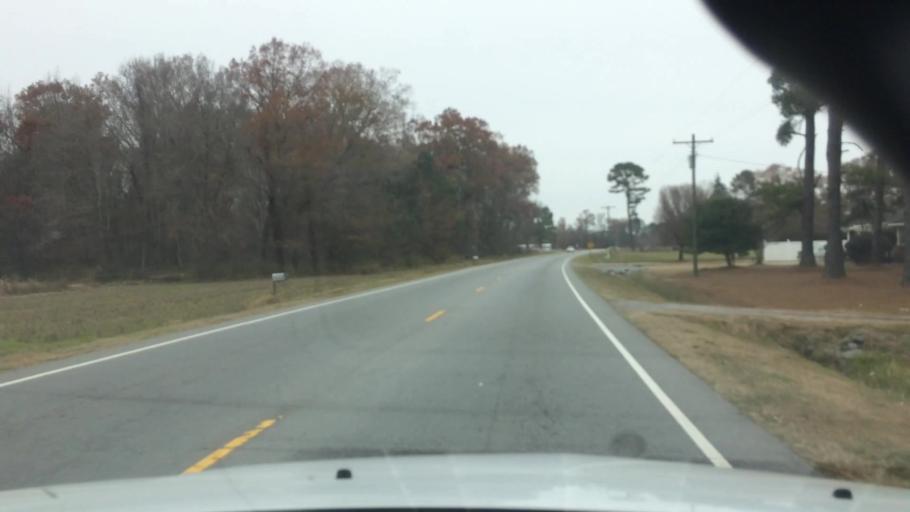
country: US
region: North Carolina
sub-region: Greene County
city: Maury
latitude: 35.5230
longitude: -77.6133
